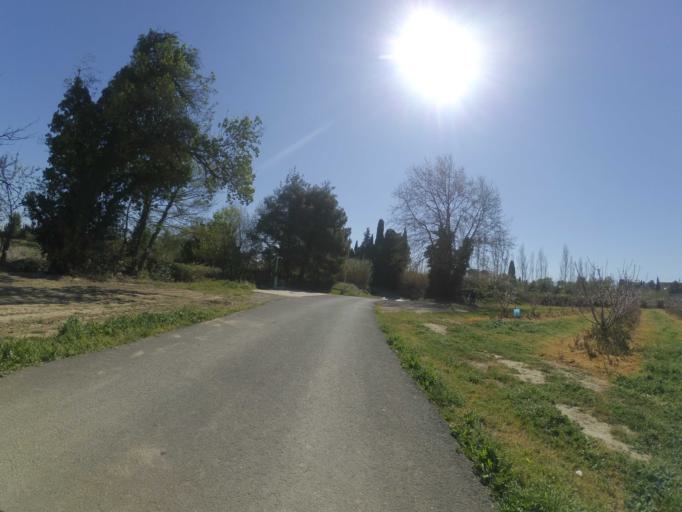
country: FR
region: Languedoc-Roussillon
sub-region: Departement des Pyrenees-Orientales
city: Corneilla-la-Riviere
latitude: 42.6835
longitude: 2.7167
